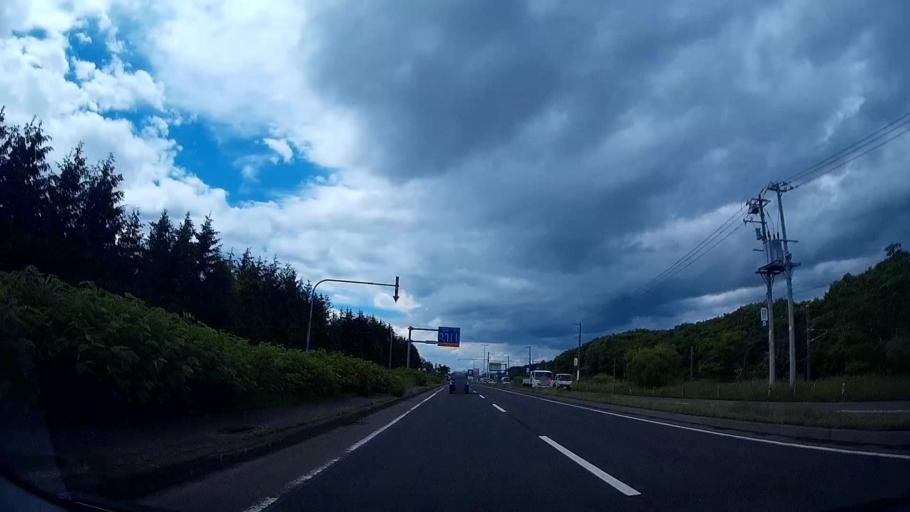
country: JP
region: Hokkaido
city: Chitose
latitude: 42.8160
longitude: 141.6654
